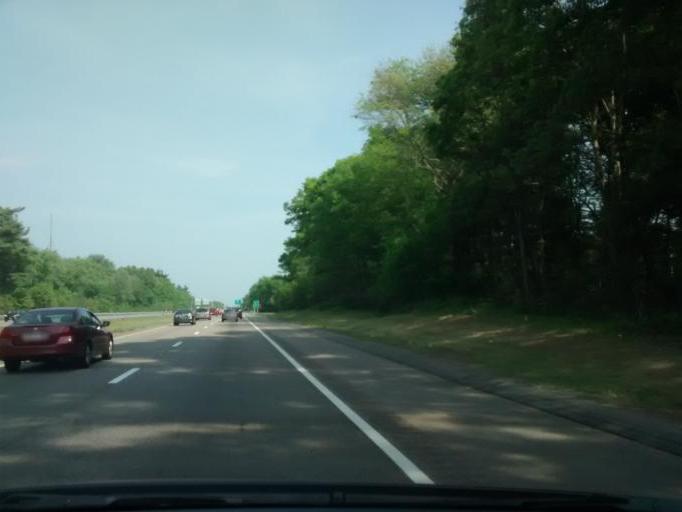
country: US
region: Massachusetts
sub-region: Plymouth County
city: Middleborough Center
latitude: 41.8948
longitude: -70.9515
